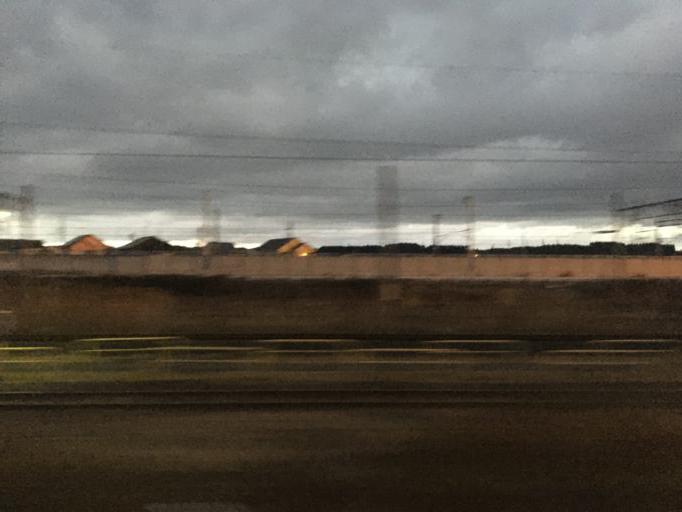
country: JP
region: Aomori
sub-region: Hachinohe Shi
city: Uchimaru
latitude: 40.5156
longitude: 141.4381
